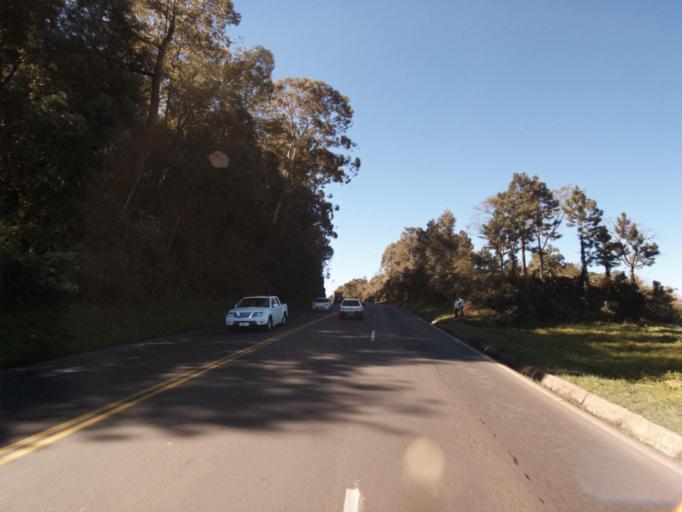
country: BR
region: Santa Catarina
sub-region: Chapeco
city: Chapeco
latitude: -26.9637
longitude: -52.5500
